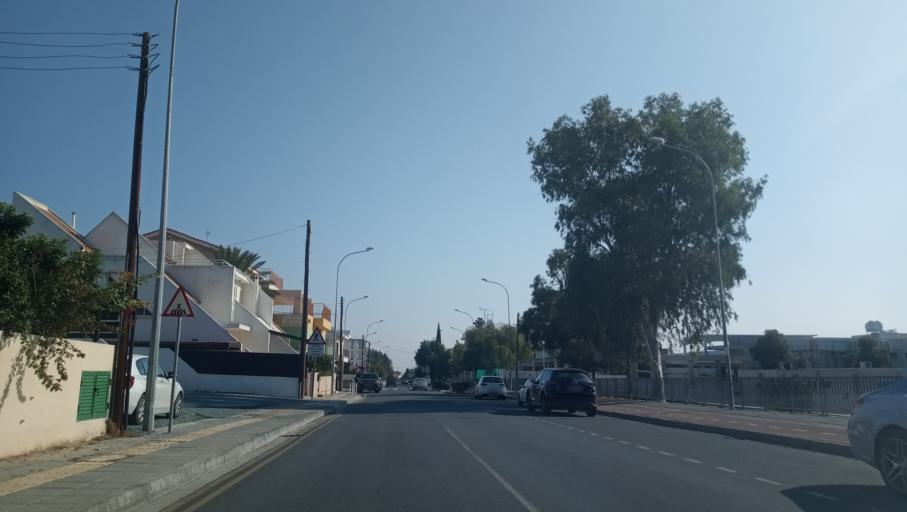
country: CY
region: Lefkosia
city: Nicosia
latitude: 35.1450
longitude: 33.3853
